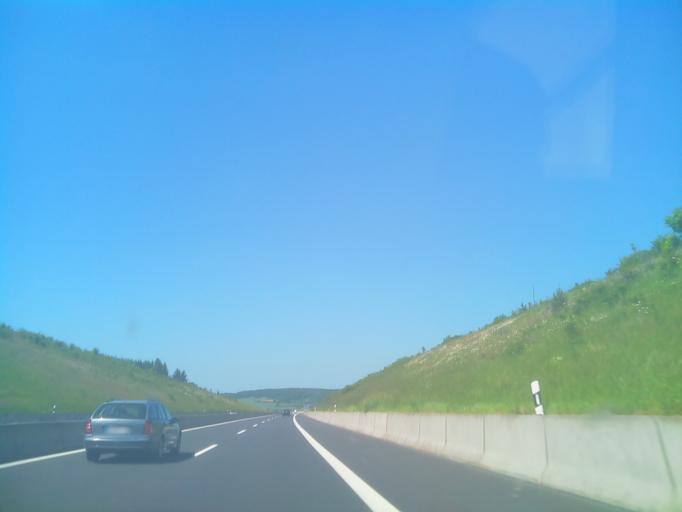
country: DE
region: Bavaria
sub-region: Regierungsbezirk Unterfranken
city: Munnerstadt
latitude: 50.2236
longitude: 10.2188
